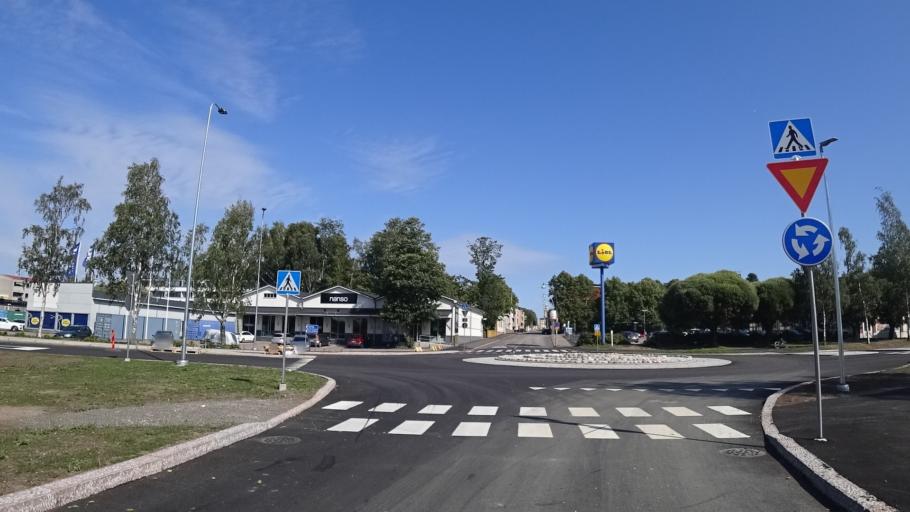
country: FI
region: Kymenlaakso
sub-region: Kotka-Hamina
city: Hamina
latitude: 60.5650
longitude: 27.1920
